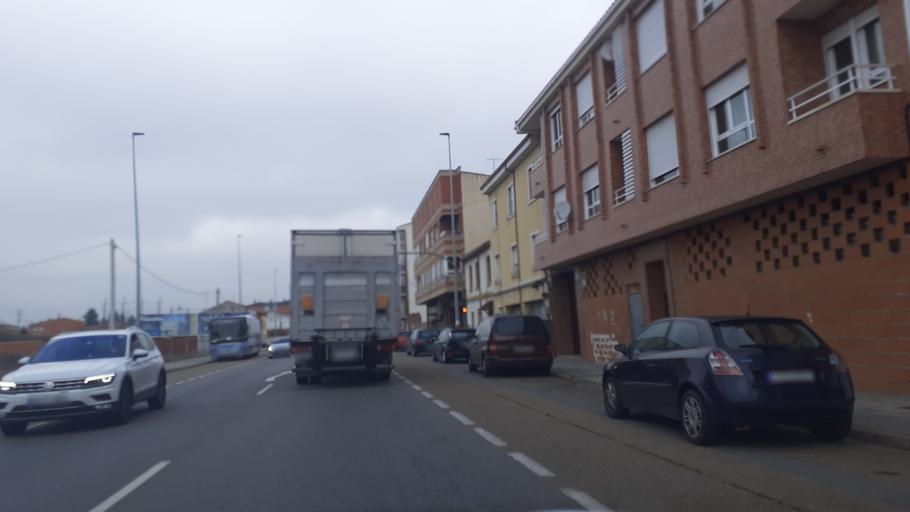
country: ES
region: Castille and Leon
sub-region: Provincia de Leon
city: Onzonilla
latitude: 42.5626
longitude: -5.5819
